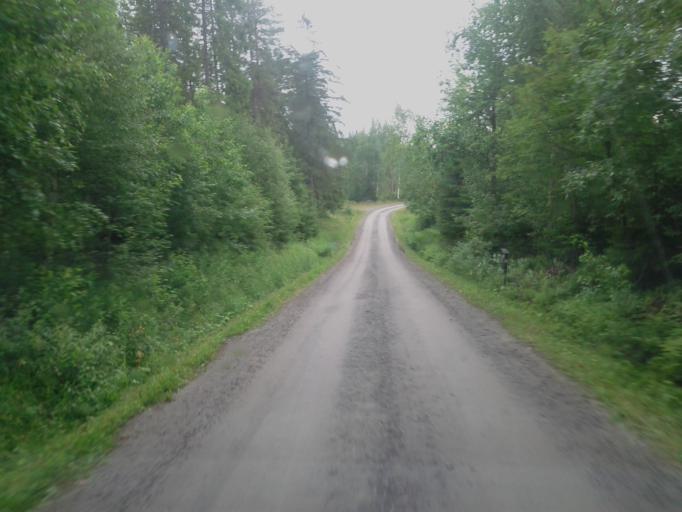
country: SE
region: Vaesternorrland
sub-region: OErnskoeldsviks Kommun
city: Bjasta
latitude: 63.0746
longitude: 18.4468
